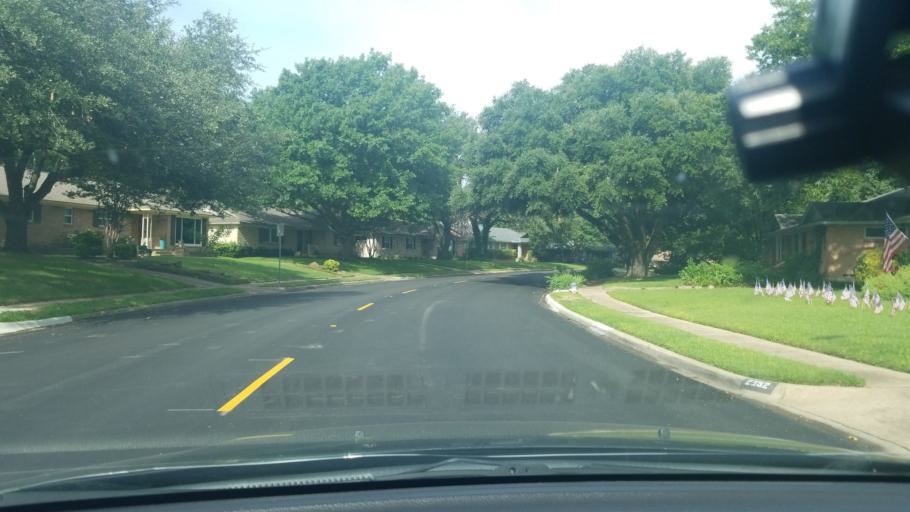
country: US
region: Texas
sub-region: Dallas County
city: Highland Park
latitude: 32.8073
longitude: -96.7034
